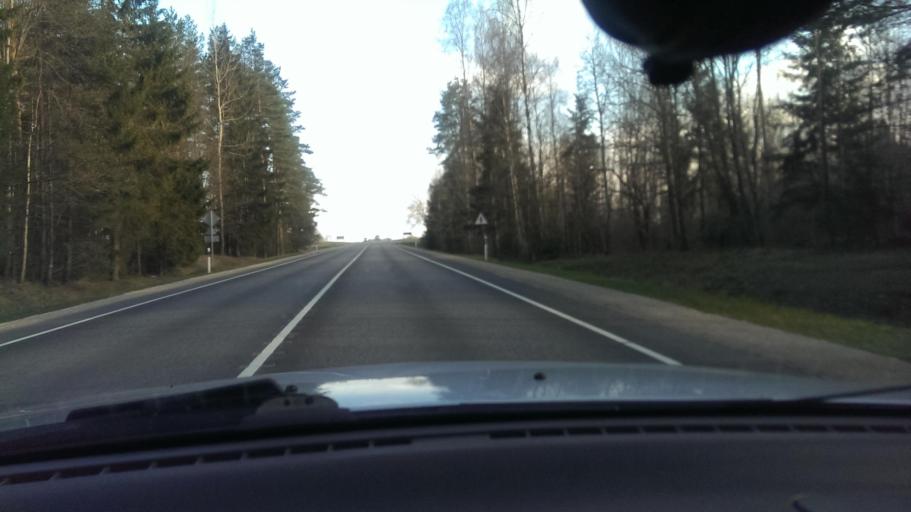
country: EE
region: Vorumaa
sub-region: Antsla vald
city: Vana-Antsla
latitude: 57.9989
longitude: 26.7623
